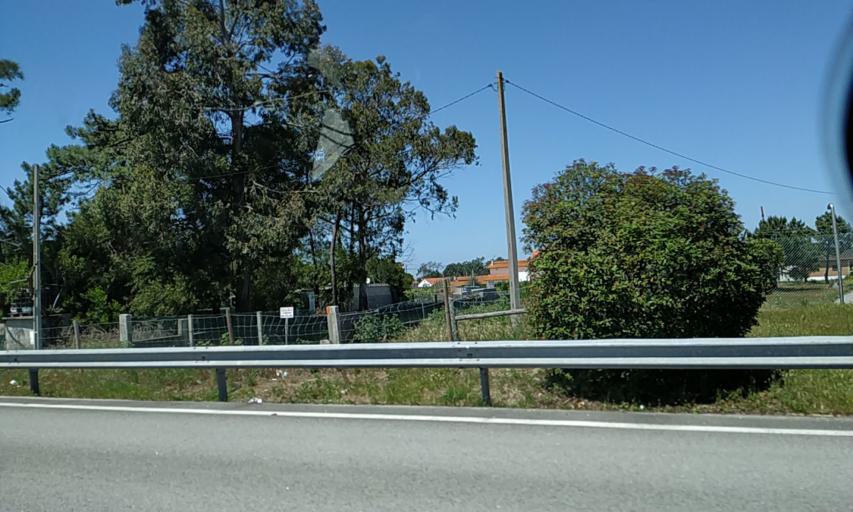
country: PT
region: Aveiro
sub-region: Ilhavo
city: Gafanha da Nazare
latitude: 40.6280
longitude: -8.7077
